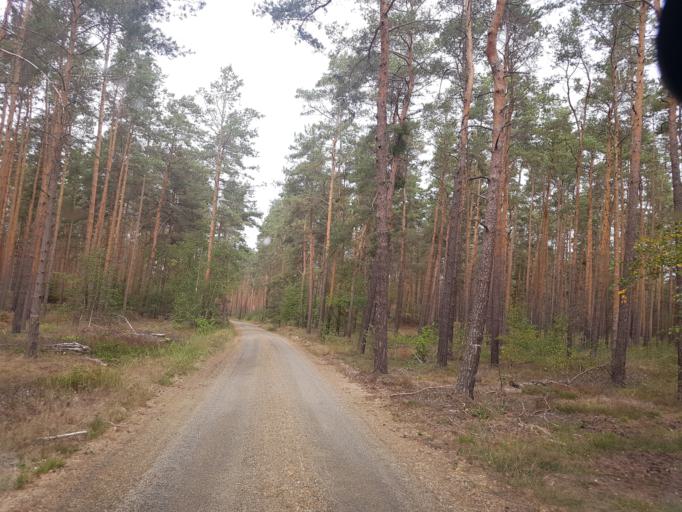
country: DE
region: Brandenburg
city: Schonborn
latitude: 51.5749
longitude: 13.4743
